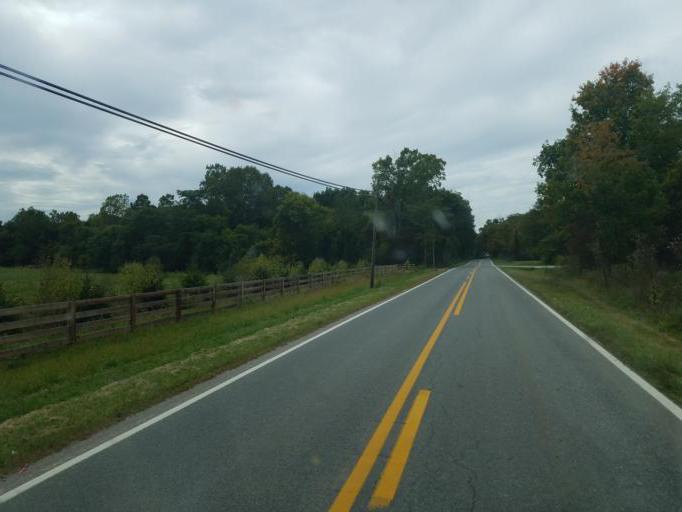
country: US
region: Ohio
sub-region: Delaware County
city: Sunbury
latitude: 40.2464
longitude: -82.8437
